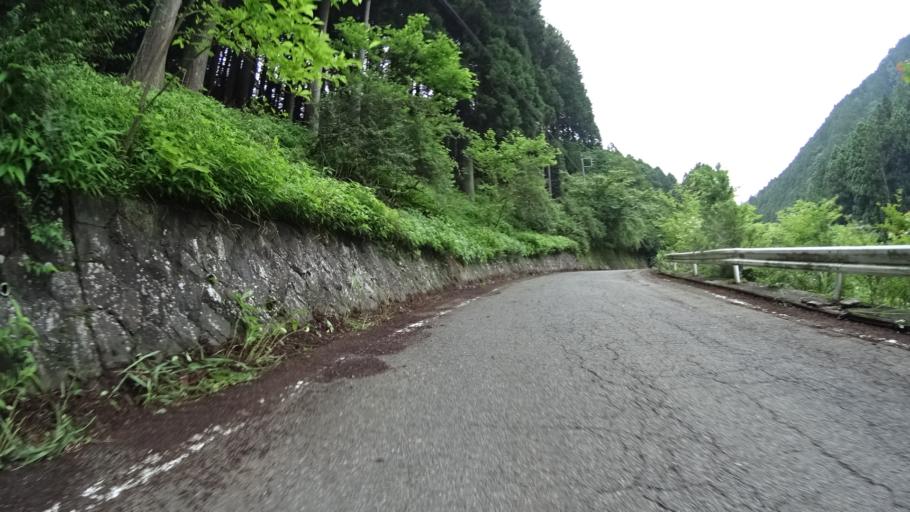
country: JP
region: Kanagawa
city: Hadano
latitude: 35.4588
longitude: 139.2136
